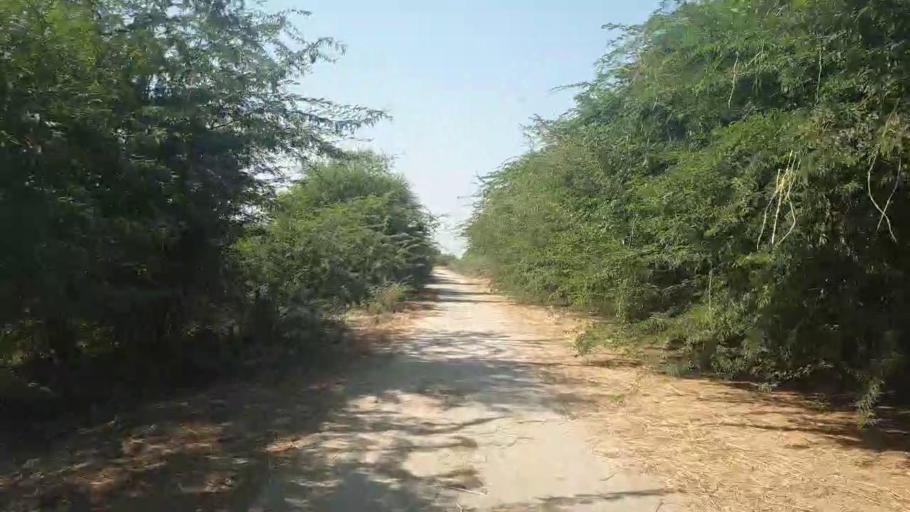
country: PK
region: Sindh
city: Badin
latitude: 24.6459
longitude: 68.9141
